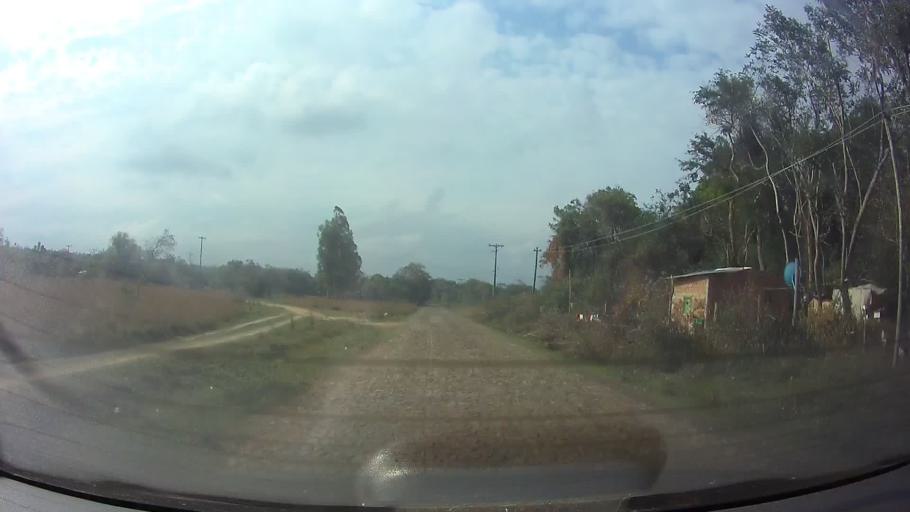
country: PY
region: Cordillera
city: Arroyos y Esteros
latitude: -25.0002
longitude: -57.1953
